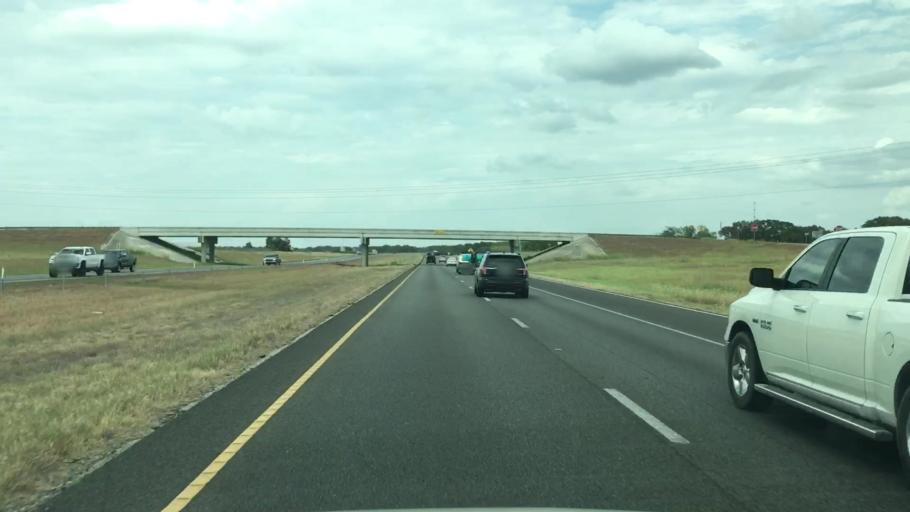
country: US
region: Texas
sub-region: Bexar County
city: Elmendorf
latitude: 29.1402
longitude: -98.4288
